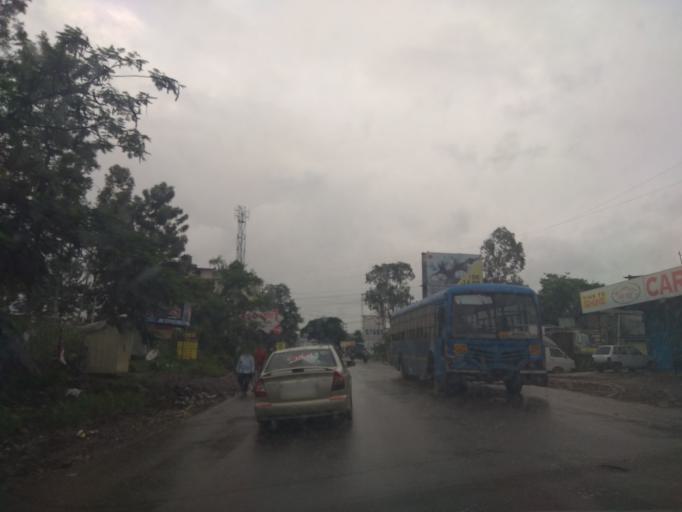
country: IN
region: Maharashtra
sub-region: Pune Division
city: Kharakvasla
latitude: 18.5120
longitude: 73.6815
